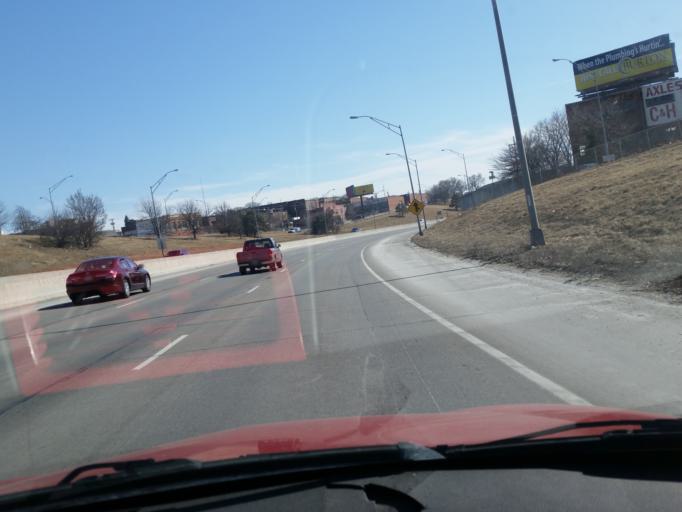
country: US
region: Nebraska
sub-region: Douglas County
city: Omaha
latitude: 41.2119
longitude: -95.9504
